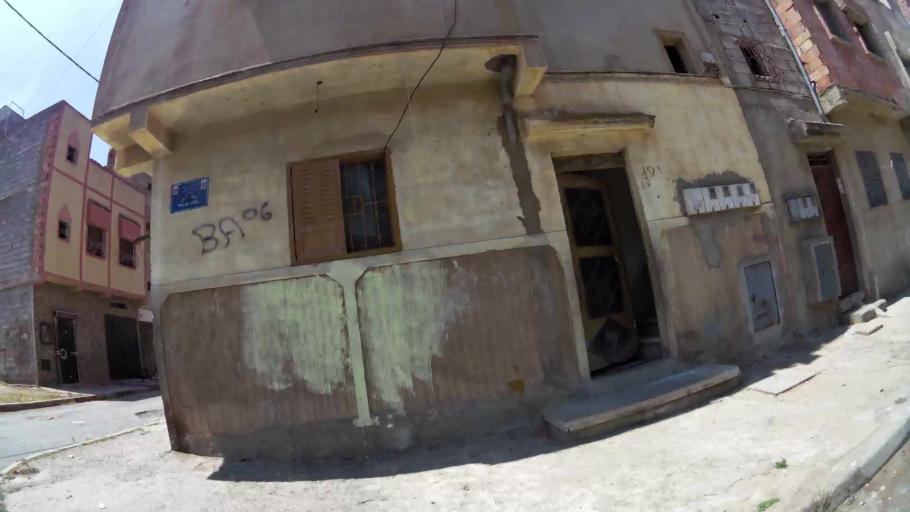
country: MA
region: Rabat-Sale-Zemmour-Zaer
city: Sale
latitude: 34.0703
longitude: -6.7827
